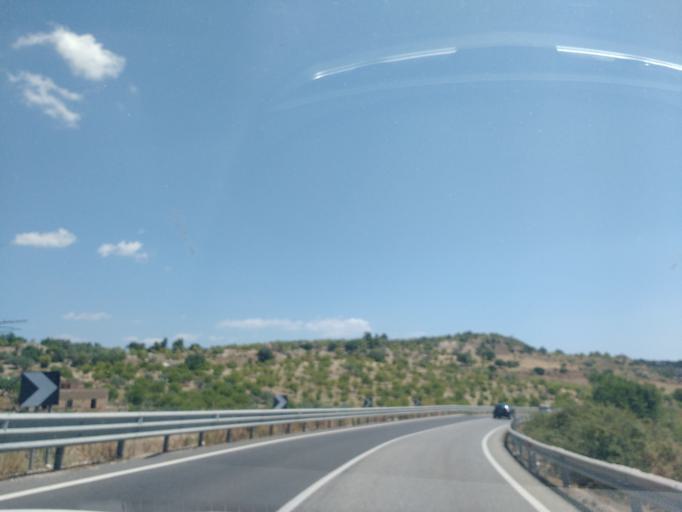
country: IT
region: Sicily
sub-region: Provincia di Siracusa
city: Noto
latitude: 36.8675
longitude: 15.0255
